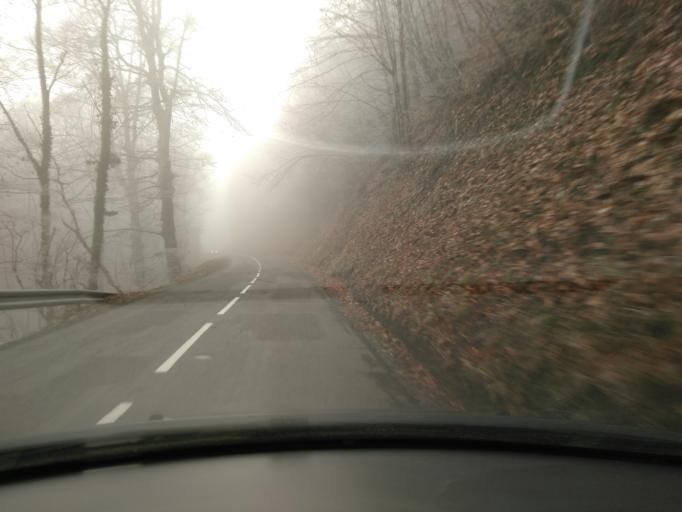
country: FR
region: Rhone-Alpes
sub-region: Departement de la Haute-Savoie
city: Sallanches
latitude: 45.9562
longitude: 6.6227
